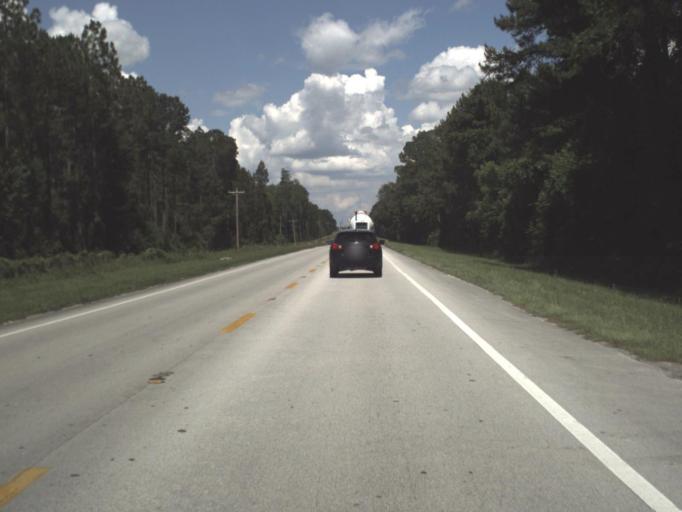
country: US
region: Florida
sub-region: Alachua County
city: Waldo
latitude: 29.7136
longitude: -82.1175
